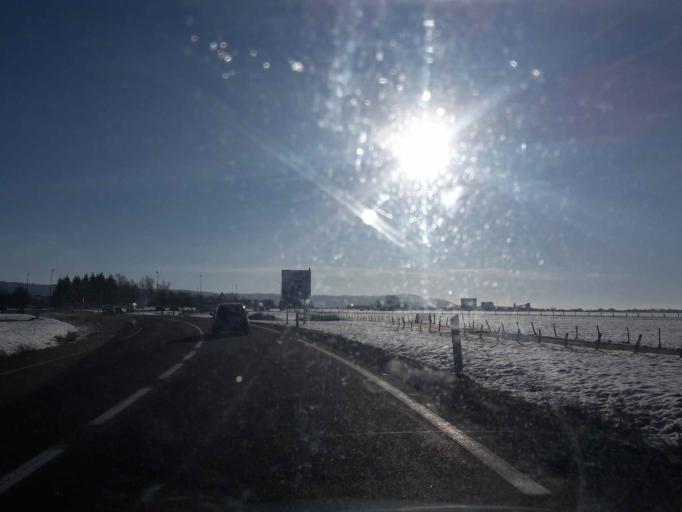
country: FR
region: Franche-Comte
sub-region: Departement du Doubs
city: Doubs
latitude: 46.9270
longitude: 6.3384
